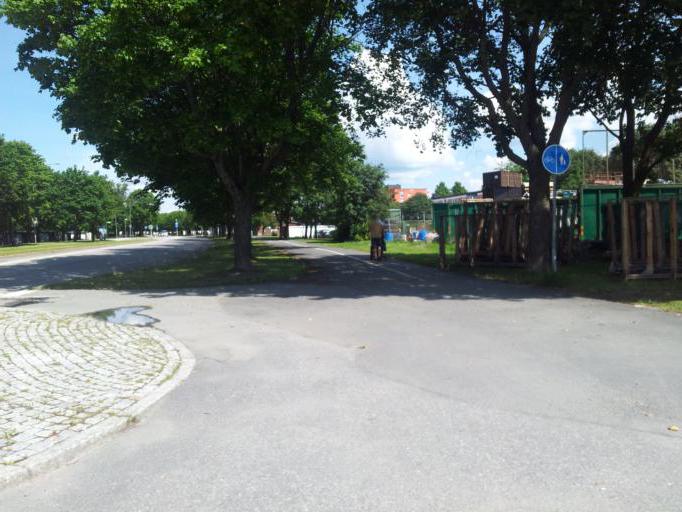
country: SE
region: Uppsala
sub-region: Uppsala Kommun
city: Uppsala
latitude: 59.8729
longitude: 17.6523
